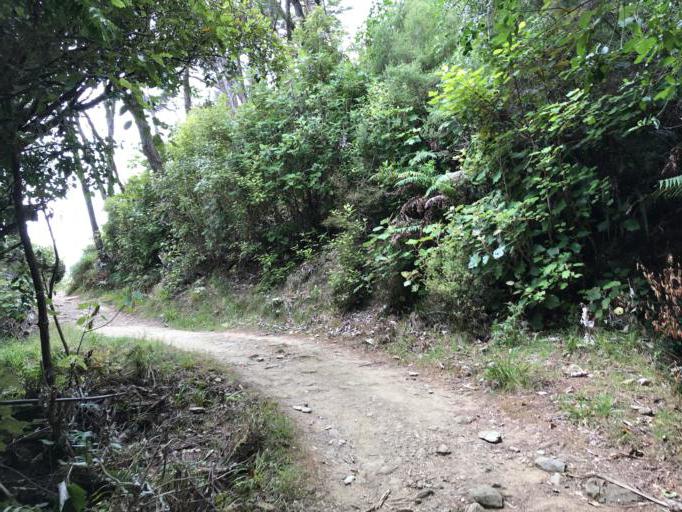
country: NZ
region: Marlborough
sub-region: Marlborough District
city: Picton
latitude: -41.1150
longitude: 174.2039
